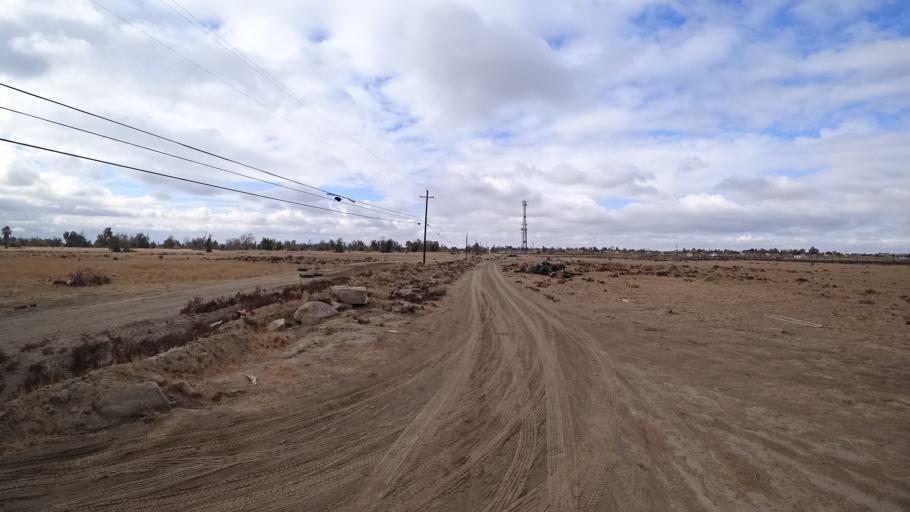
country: US
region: California
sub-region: Kern County
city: Bakersfield
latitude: 35.3395
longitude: -118.9770
